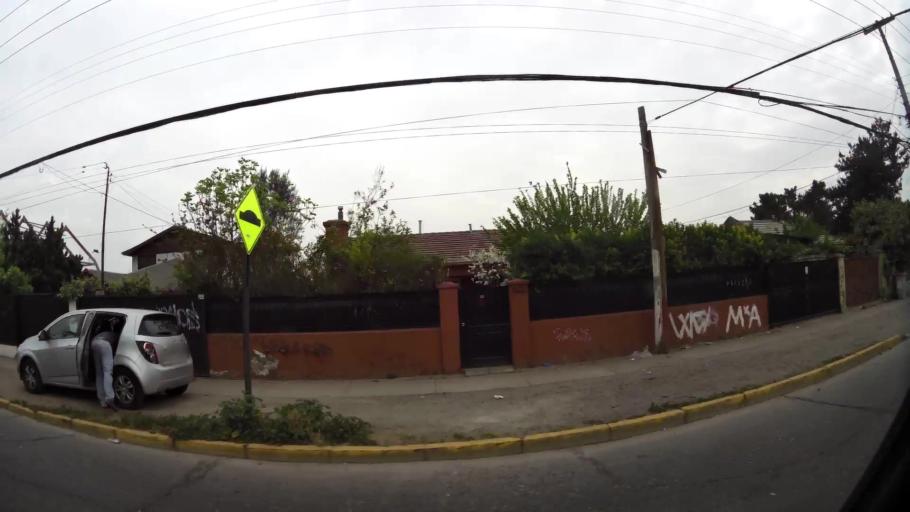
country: CL
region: Santiago Metropolitan
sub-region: Provincia de Santiago
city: Lo Prado
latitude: -33.5012
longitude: -70.7522
